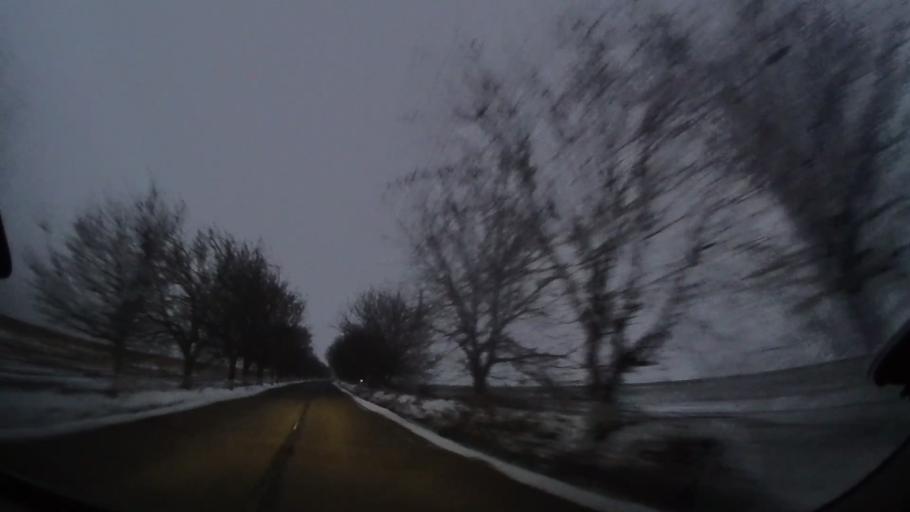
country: RO
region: Vaslui
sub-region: Comuna Dimitrie Cantemir
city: Dimitrie Cantemir
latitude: 46.5104
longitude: 28.0363
